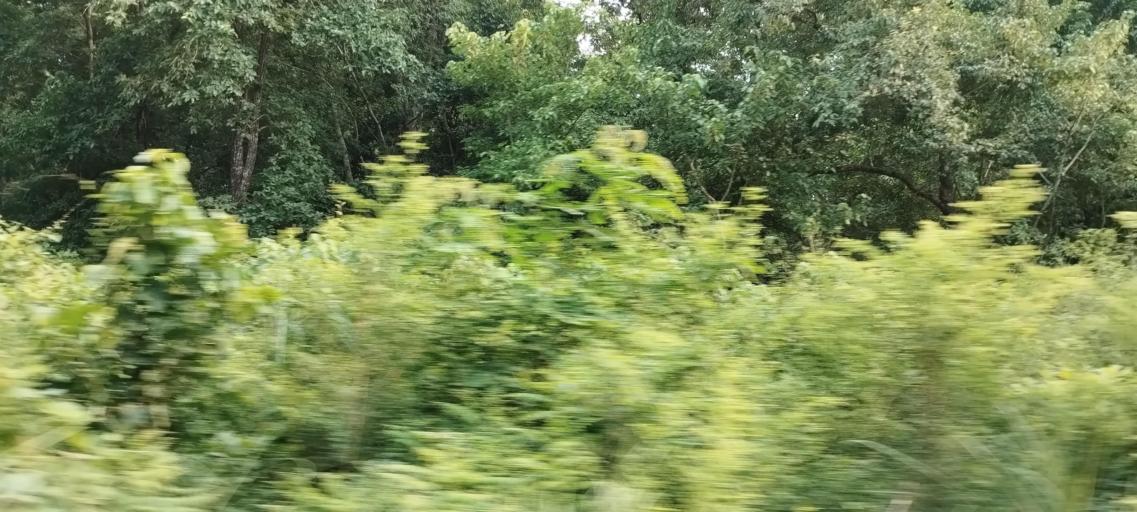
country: NP
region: Mid Western
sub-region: Bheri Zone
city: Bardiya
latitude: 28.4298
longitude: 81.3465
